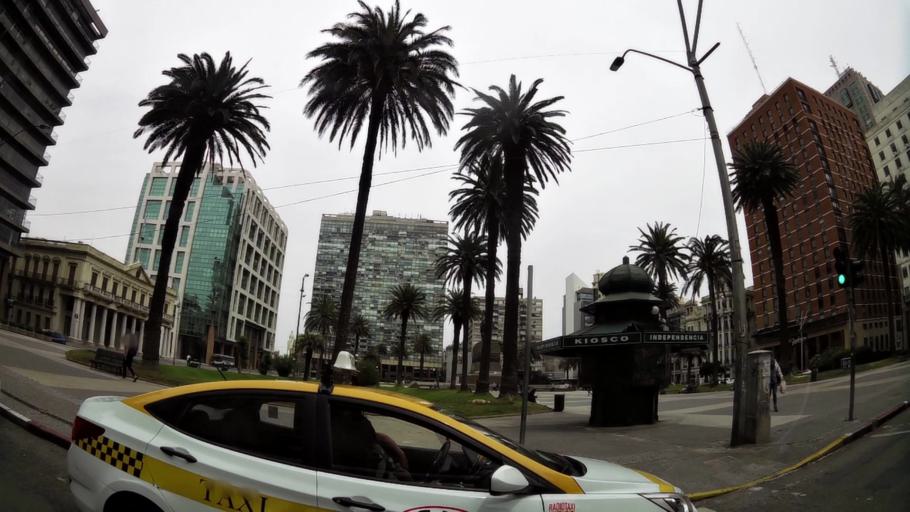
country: UY
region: Montevideo
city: Montevideo
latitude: -34.9066
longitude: -56.1987
